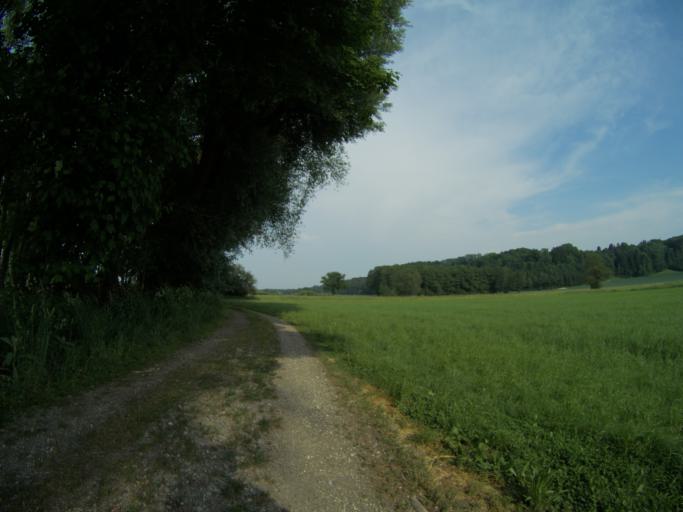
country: DE
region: Bavaria
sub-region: Upper Bavaria
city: Zolling
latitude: 48.4415
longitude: 11.7688
